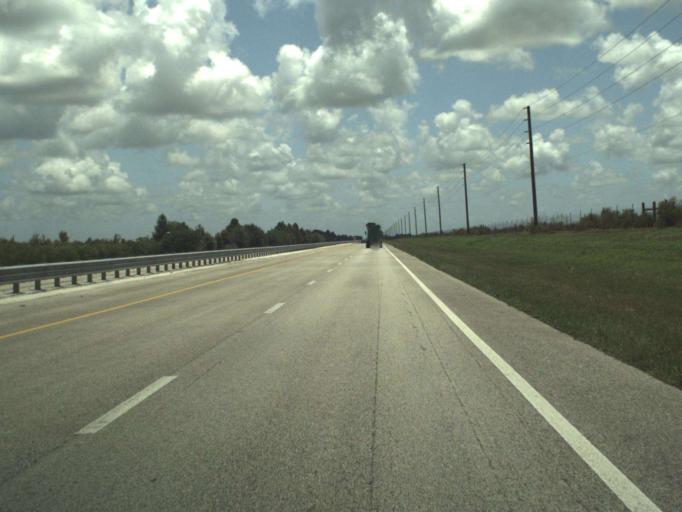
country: US
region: Florida
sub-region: Indian River County
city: Fellsmere
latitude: 27.6408
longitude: -80.6974
